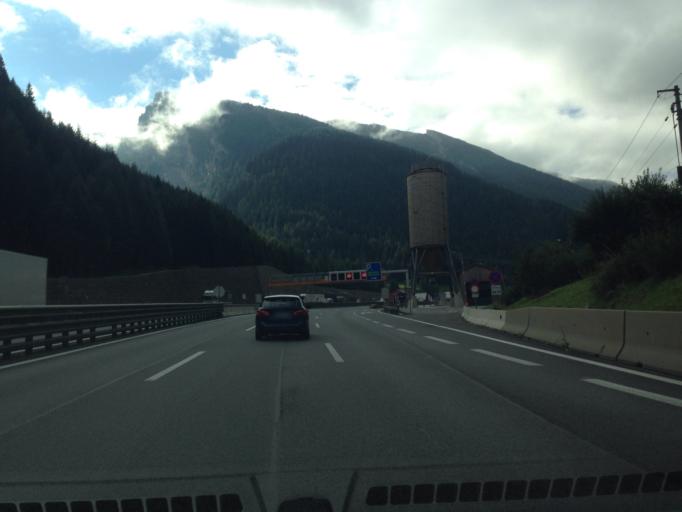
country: AT
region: Tyrol
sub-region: Politischer Bezirk Innsbruck Land
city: Gries am Brenner
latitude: 47.0115
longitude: 11.5074
